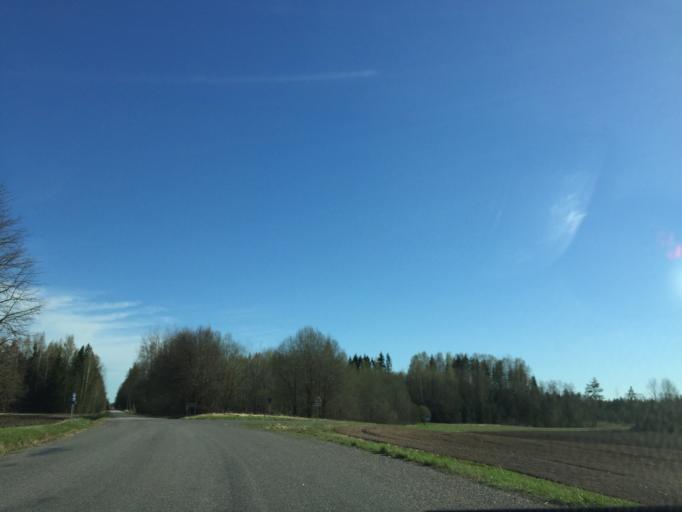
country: EE
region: Valgamaa
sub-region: Valga linn
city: Valga
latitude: 57.8512
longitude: 26.2530
